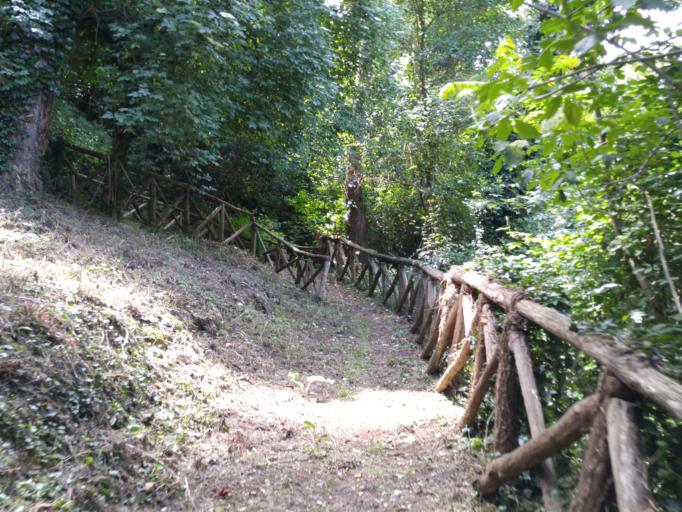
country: IT
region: The Marches
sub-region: Provincia di Pesaro e Urbino
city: Montemaggiore al Metauro
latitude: 43.7385
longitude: 12.9475
